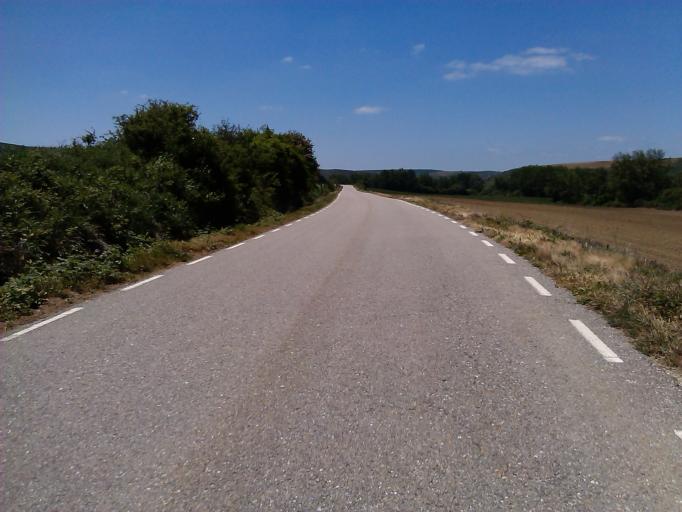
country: ES
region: Castille and Leon
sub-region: Provincia de Burgos
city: Arraya de Oca
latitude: 42.4240
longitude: -3.3926
